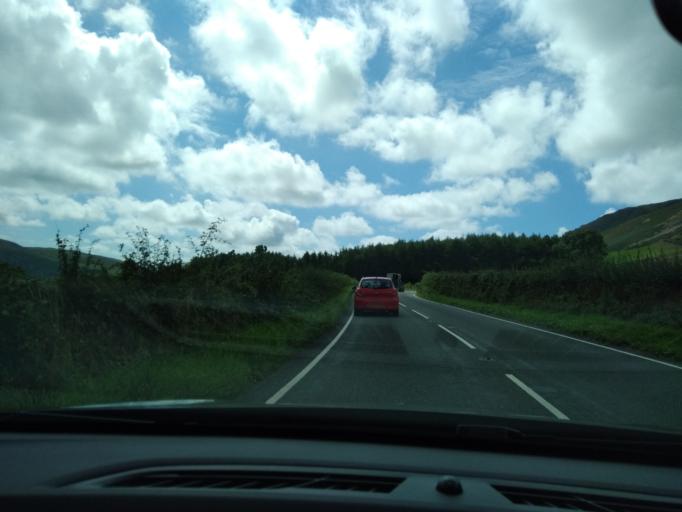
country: GB
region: England
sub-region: Cumbria
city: Millom
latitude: 54.2483
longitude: -3.3070
